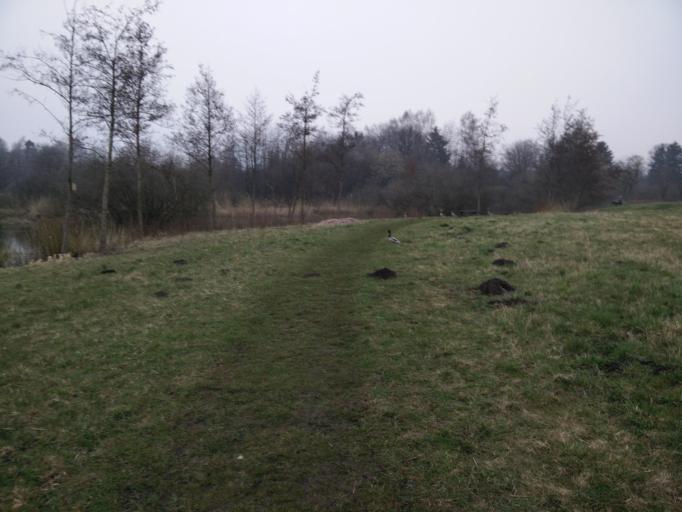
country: DK
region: Capital Region
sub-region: Herlev Kommune
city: Herlev
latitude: 55.7516
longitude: 12.4271
